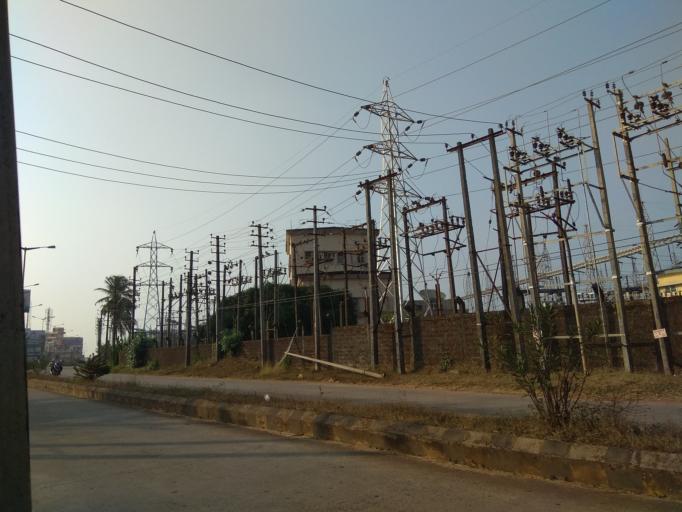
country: IN
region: Karnataka
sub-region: Dakshina Kannada
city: Mangalore
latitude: 12.9246
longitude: 74.8614
